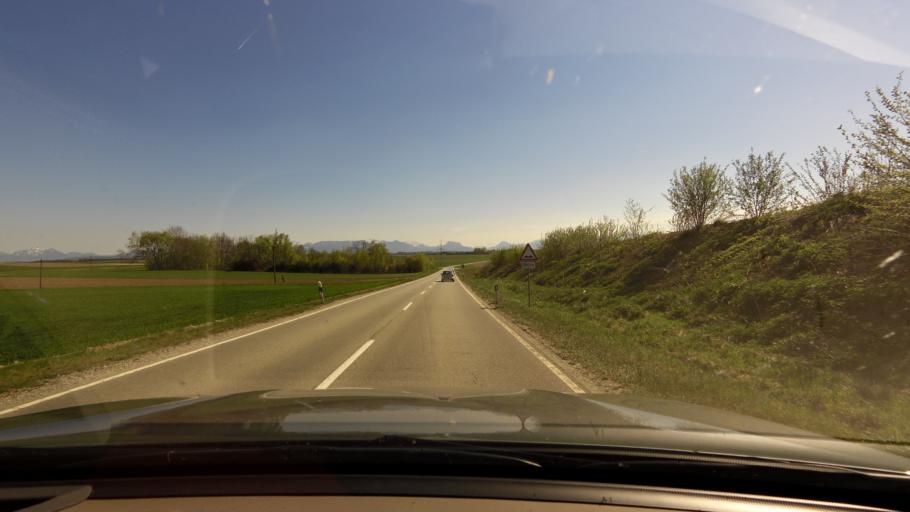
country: DE
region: Bavaria
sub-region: Upper Bavaria
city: Griesstatt
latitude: 47.9815
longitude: 12.1773
